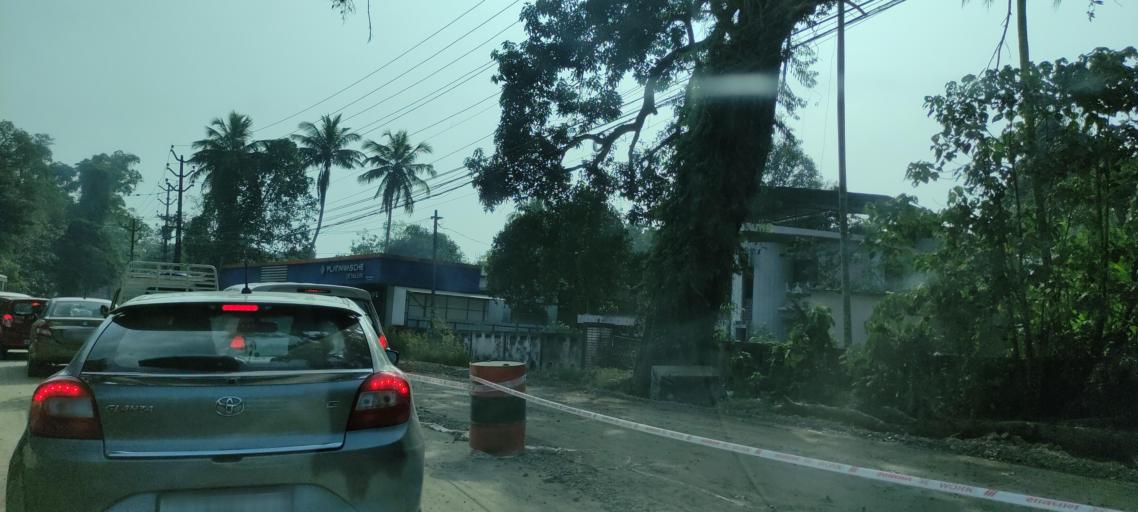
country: IN
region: Kerala
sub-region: Pattanamtitta
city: Tiruvalla
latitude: 9.3680
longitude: 76.5469
